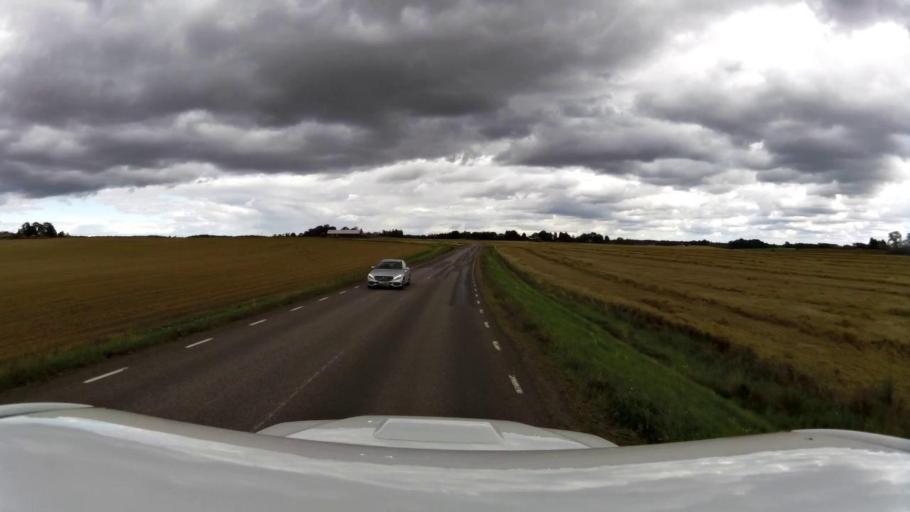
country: SE
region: OEstergoetland
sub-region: Linkopings Kommun
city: Linghem
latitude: 58.3902
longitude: 15.7505
